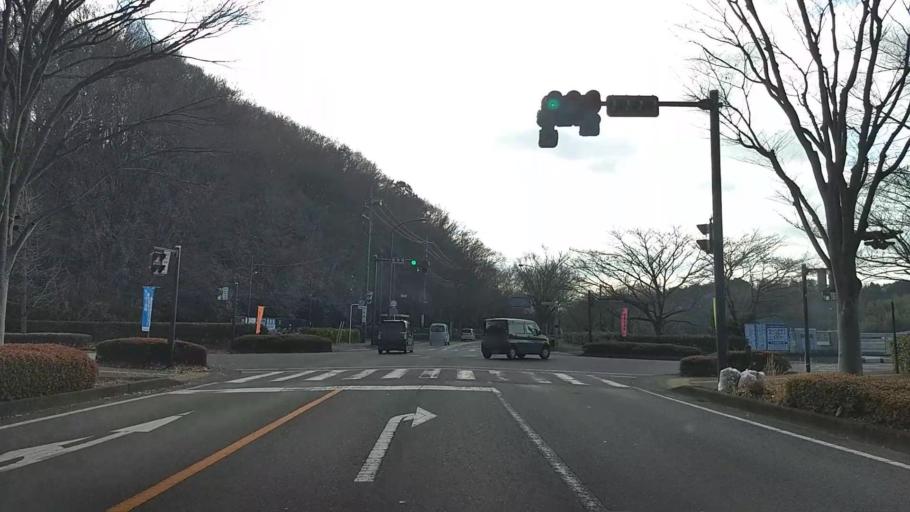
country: JP
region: Kanagawa
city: Atsugi
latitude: 35.4421
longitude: 139.3120
